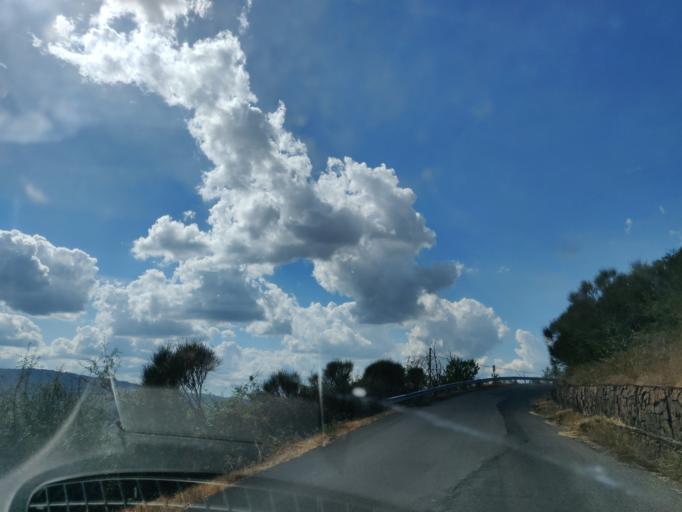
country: IT
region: Tuscany
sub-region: Provincia di Siena
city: Radicofani
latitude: 42.9547
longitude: 11.7270
